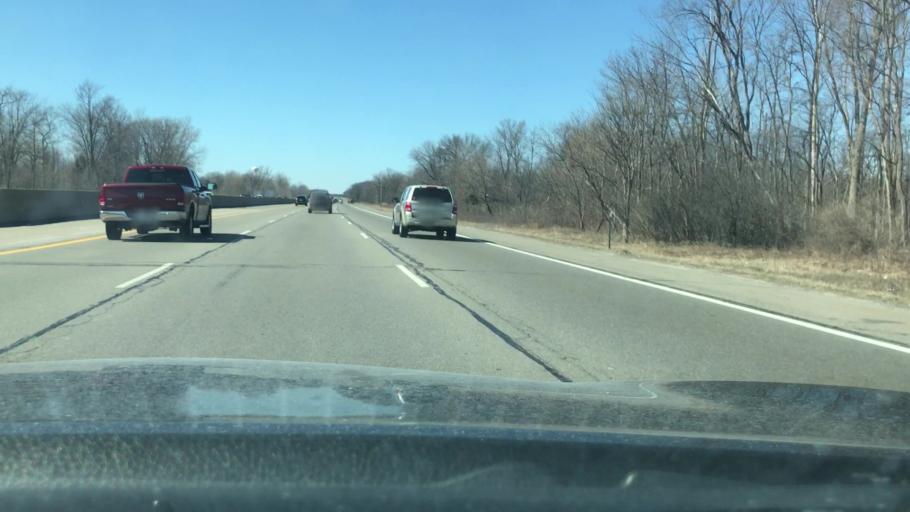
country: US
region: Michigan
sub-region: Oakland County
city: Wixom
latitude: 42.5025
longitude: -83.5565
